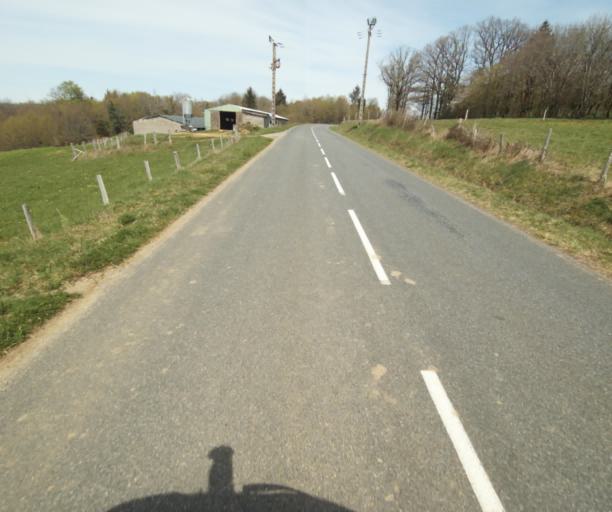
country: FR
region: Limousin
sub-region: Departement de la Correze
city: Naves
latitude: 45.3667
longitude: 1.7959
